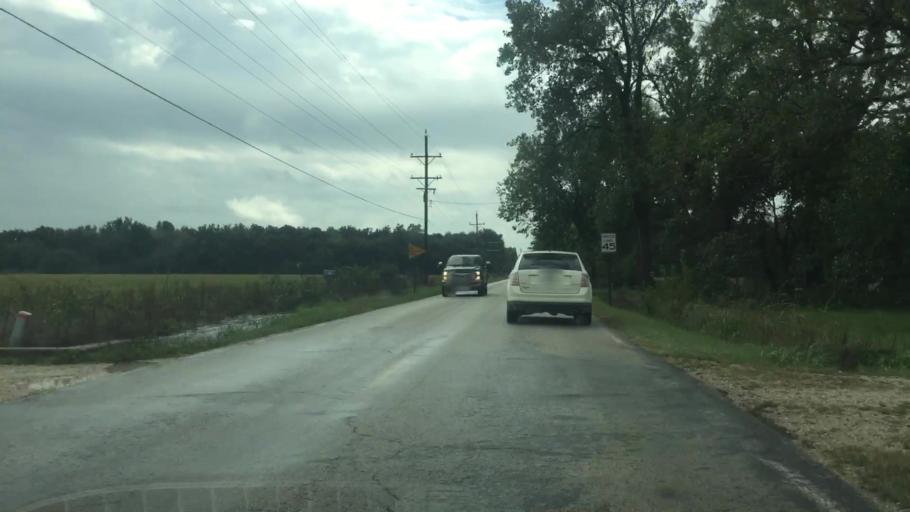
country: US
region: Kansas
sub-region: Allen County
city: Humboldt
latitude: 37.8711
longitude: -95.4369
